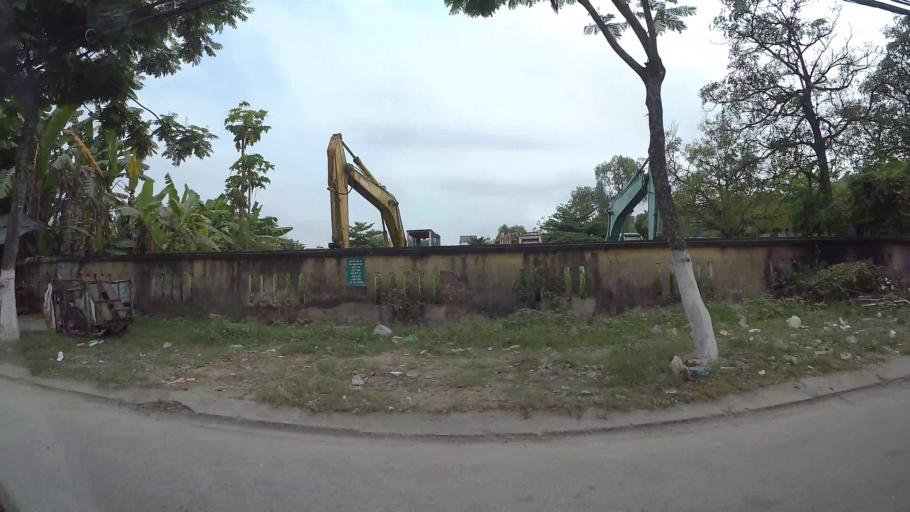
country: VN
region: Da Nang
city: Cam Le
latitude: 16.0348
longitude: 108.1792
